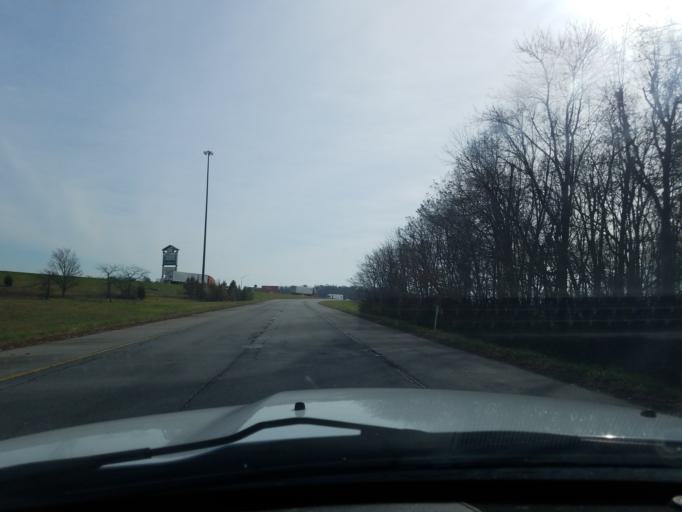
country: US
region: Indiana
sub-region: Delaware County
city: Daleville
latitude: 40.1128
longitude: -85.5703
